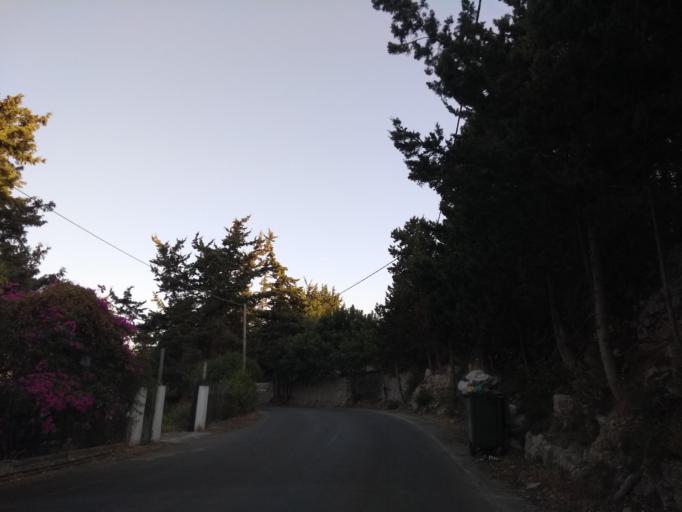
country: GR
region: Crete
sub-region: Nomos Chanias
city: Kalivai
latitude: 35.4328
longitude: 24.1796
